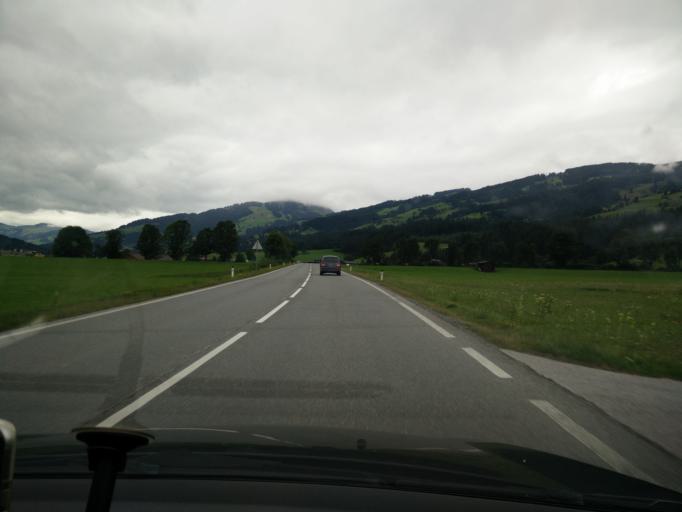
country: AT
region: Tyrol
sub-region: Politischer Bezirk Kitzbuhel
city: Kirchberg in Tirol
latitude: 47.4515
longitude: 12.2985
